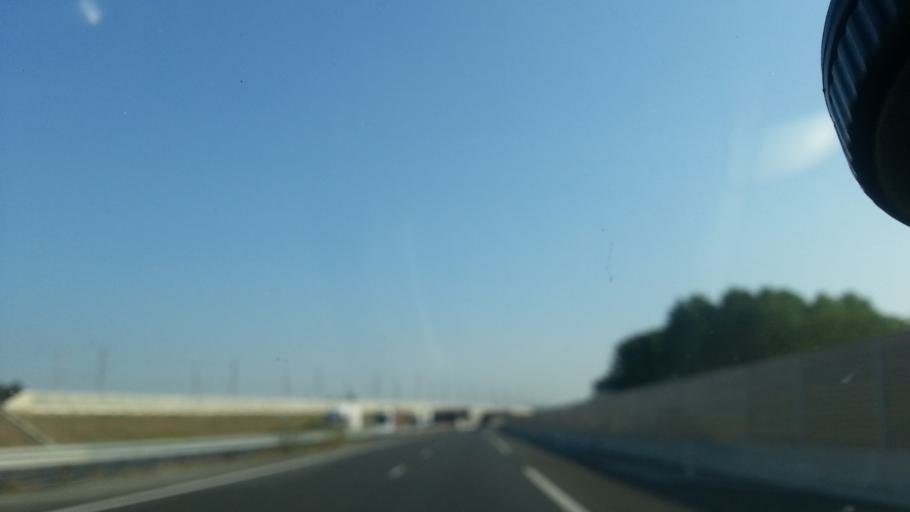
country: FR
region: Centre
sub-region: Departement d'Indre-et-Loire
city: La Celle-Saint-Avant
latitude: 47.0001
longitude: 0.5526
